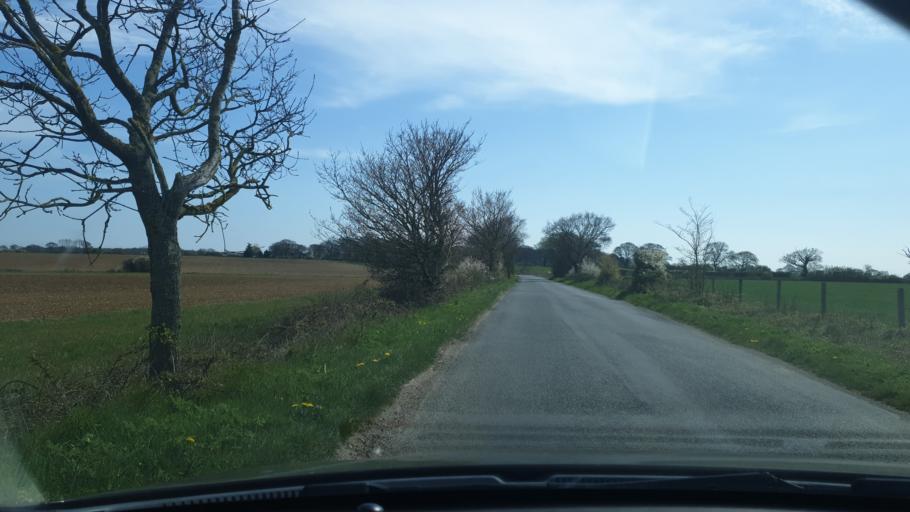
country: GB
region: England
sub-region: Essex
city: Great Bentley
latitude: 51.8509
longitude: 1.0867
